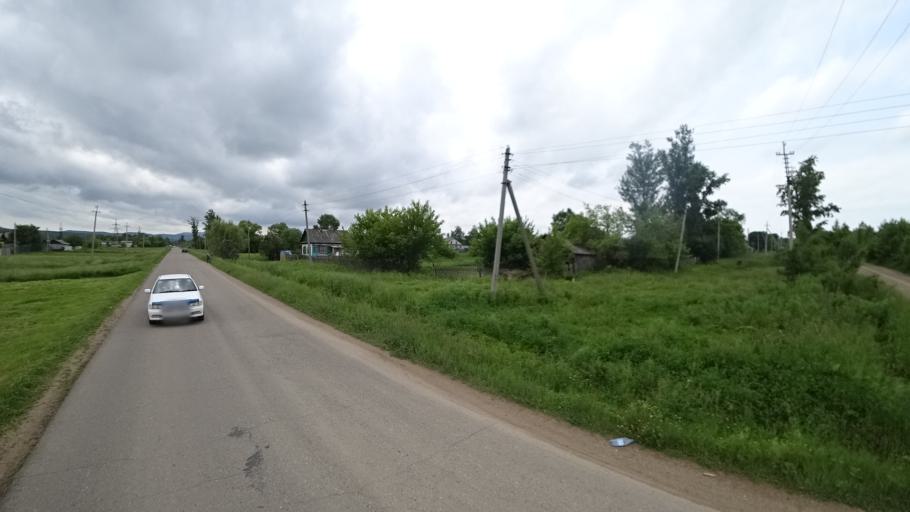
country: RU
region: Primorskiy
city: Novosysoyevka
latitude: 44.2371
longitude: 133.3695
